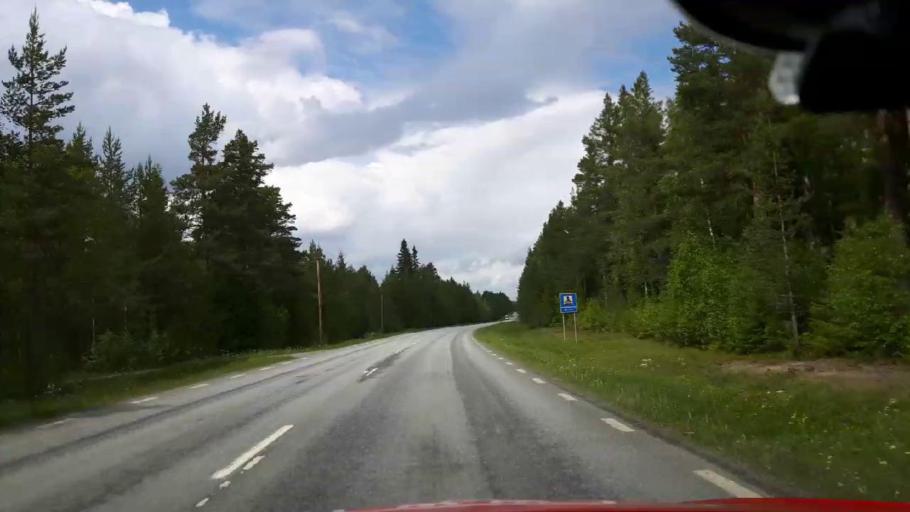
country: SE
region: Jaemtland
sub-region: Krokoms Kommun
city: Krokom
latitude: 63.3617
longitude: 14.3990
